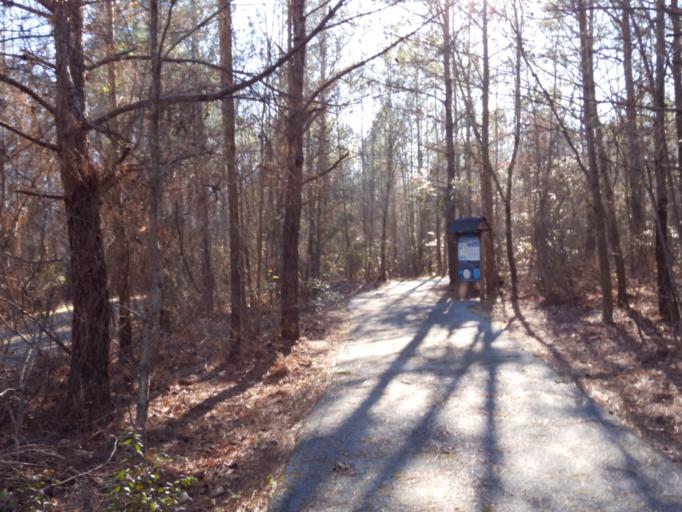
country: US
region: North Carolina
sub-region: Nash County
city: Red Oak
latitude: 36.2633
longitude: -77.8885
